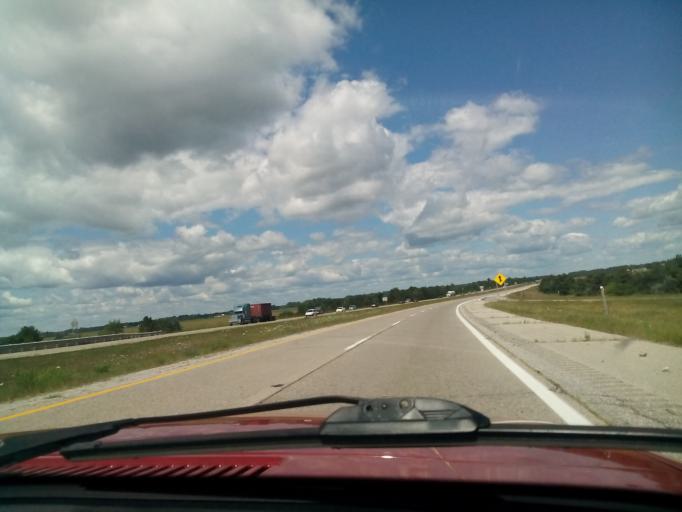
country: US
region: Michigan
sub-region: Bay County
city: Auburn
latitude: 43.6690
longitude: -84.0125
